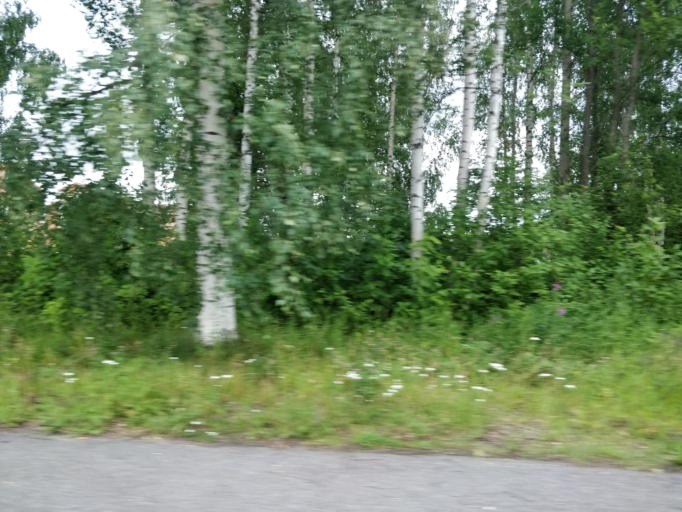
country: SE
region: Vaesterbotten
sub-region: Skelleftea Kommun
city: Viken
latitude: 64.7582
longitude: 20.9016
